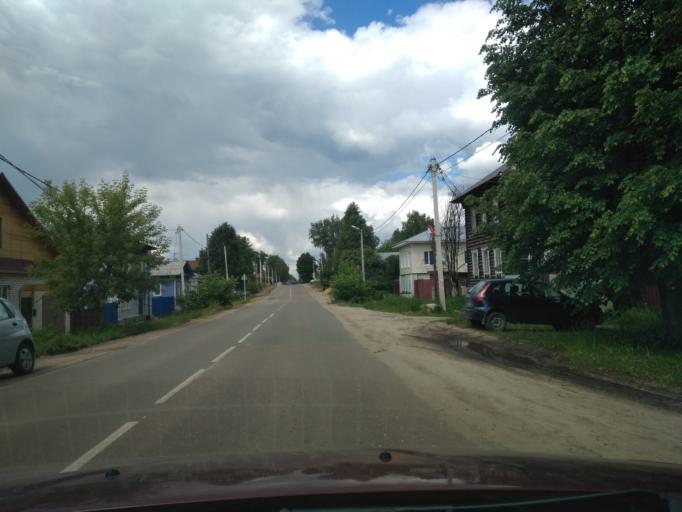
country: RU
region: Vladimir
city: Melenki
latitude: 55.3391
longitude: 41.6270
